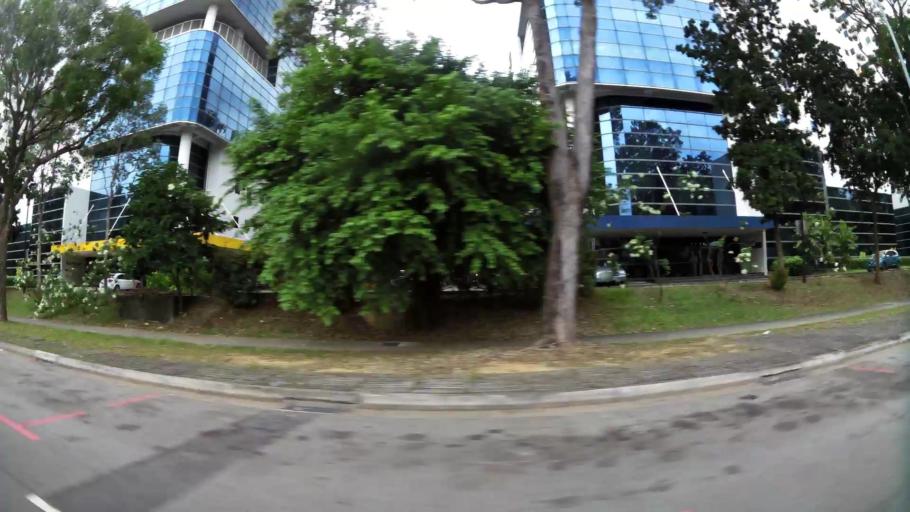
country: MY
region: Johor
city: Johor Bahru
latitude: 1.4536
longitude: 103.8083
